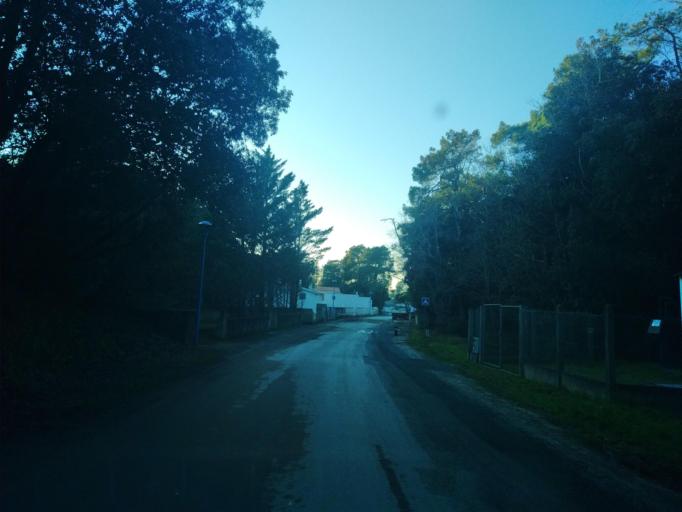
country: FR
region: Pays de la Loire
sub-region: Departement de la Vendee
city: Longeville-sur-Mer
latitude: 46.3882
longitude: -1.4746
